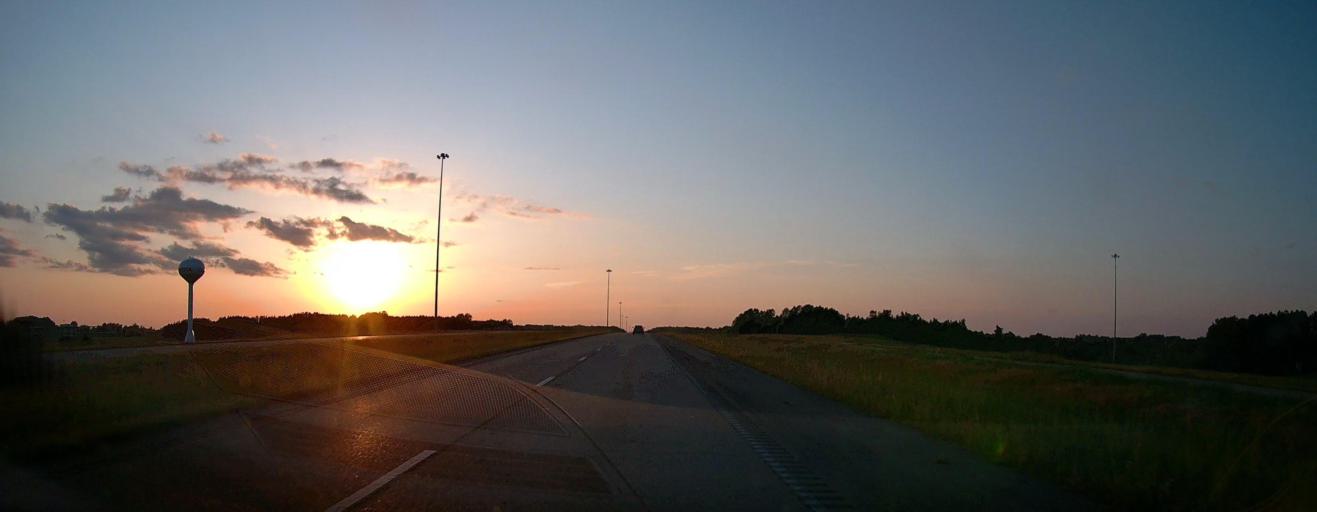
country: US
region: Mississippi
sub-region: Union County
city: New Albany
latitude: 34.3872
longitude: -88.8917
